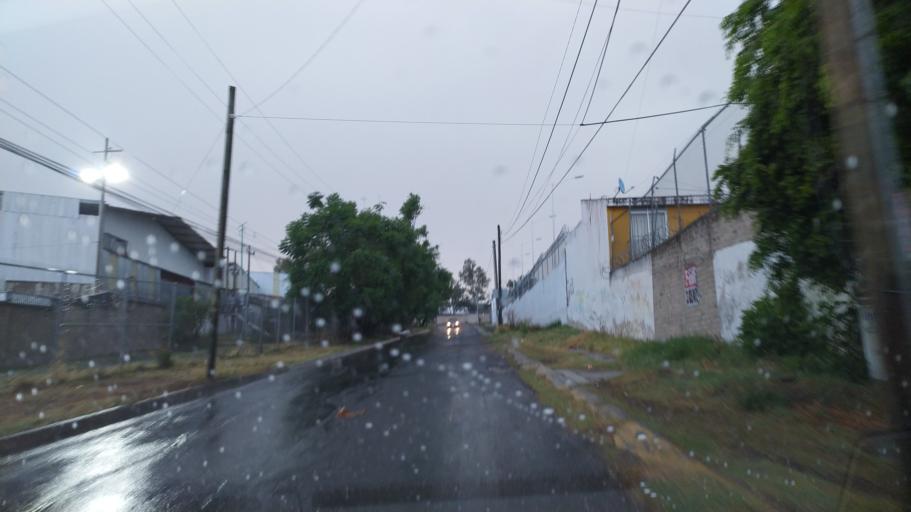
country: MX
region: Jalisco
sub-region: San Pedro Tlaquepaque
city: Paseo del Prado
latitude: 20.6085
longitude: -103.3975
